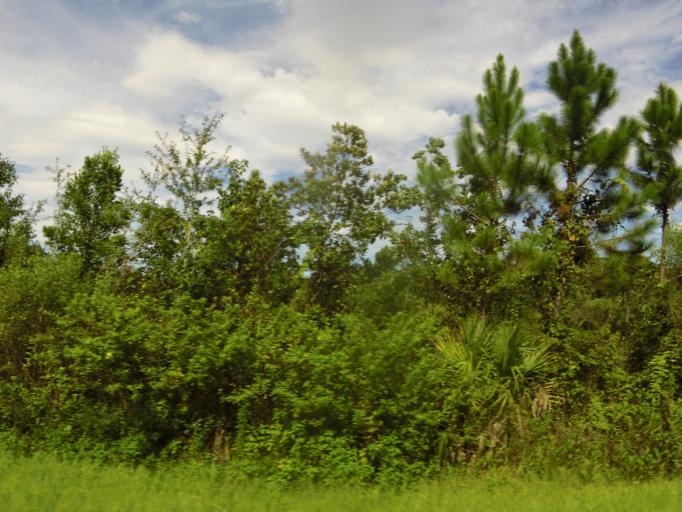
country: US
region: Florida
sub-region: Clay County
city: Green Cove Springs
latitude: 29.9568
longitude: -81.6678
